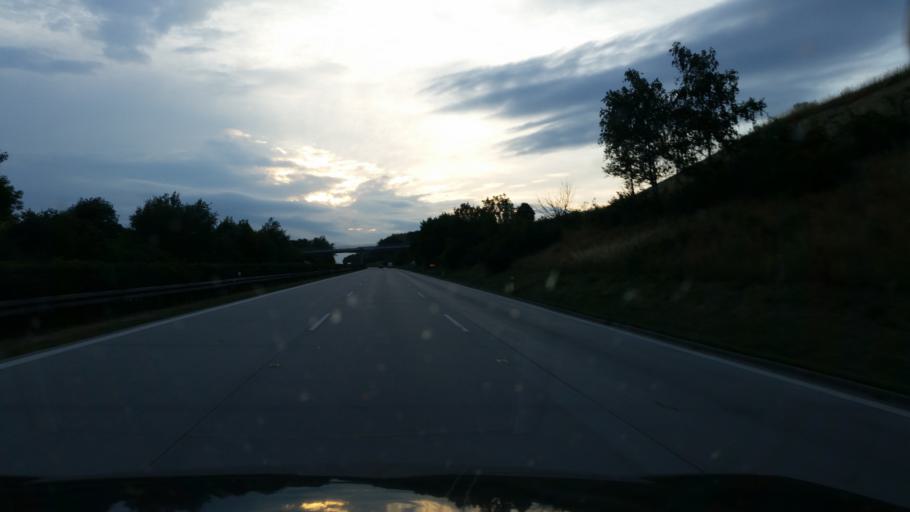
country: CZ
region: Olomoucky
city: Dolni Ujezd
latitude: 49.5536
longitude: 17.5286
